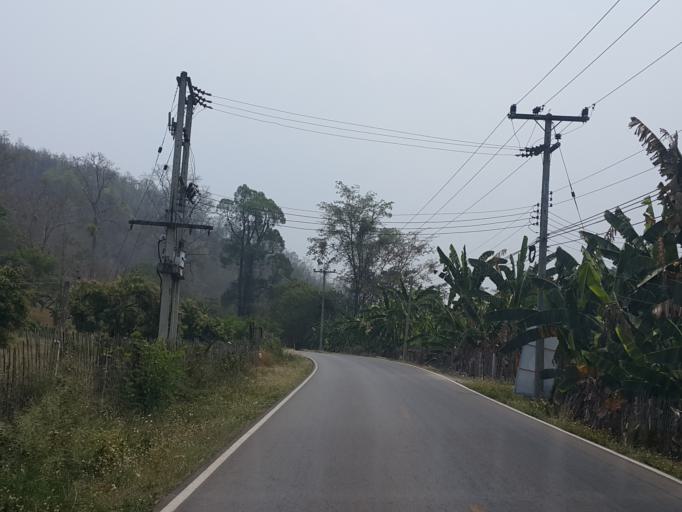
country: TH
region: Chiang Mai
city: Mae Taeng
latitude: 19.0046
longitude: 98.8863
